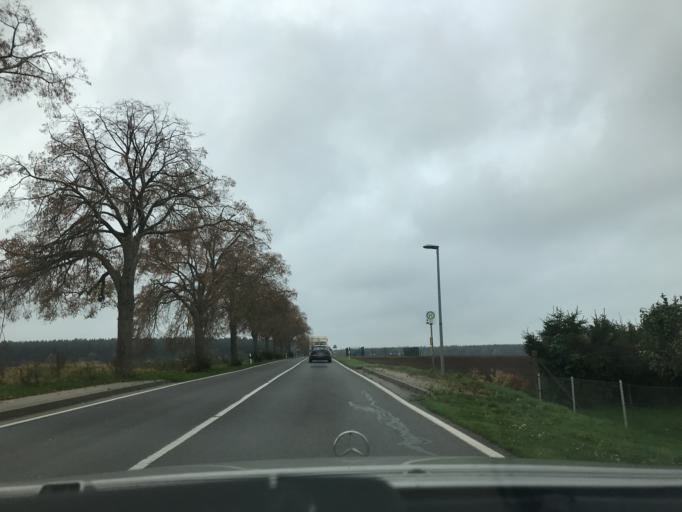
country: DE
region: Mecklenburg-Vorpommern
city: Wolgast
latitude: 54.0368
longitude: 13.7051
